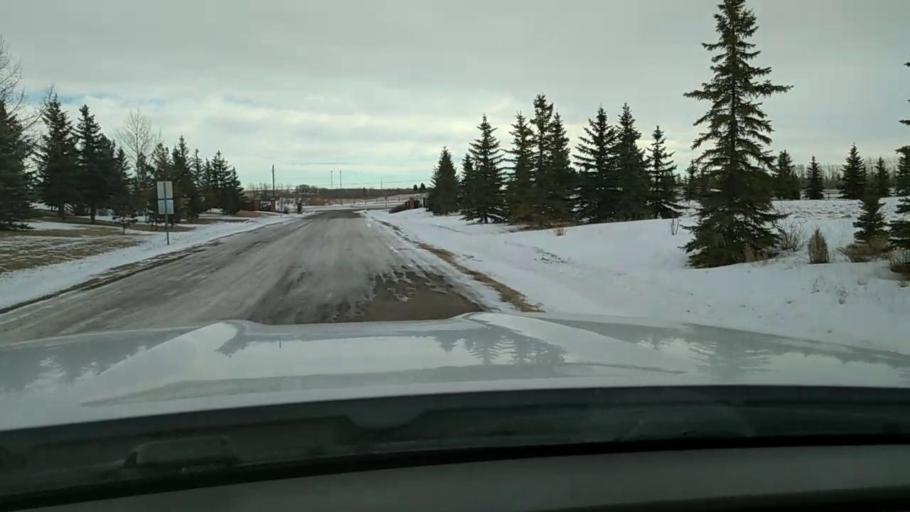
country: CA
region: Alberta
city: Cochrane
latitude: 51.2049
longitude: -114.2826
